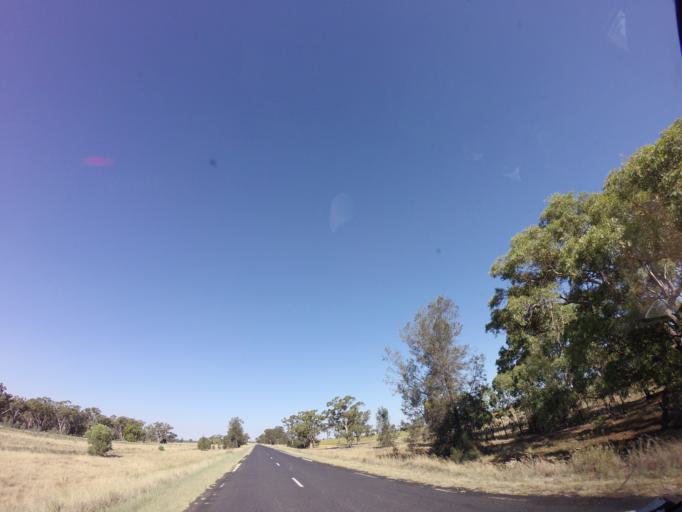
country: AU
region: New South Wales
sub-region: Gilgandra
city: Gilgandra
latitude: -31.6598
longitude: 148.4377
